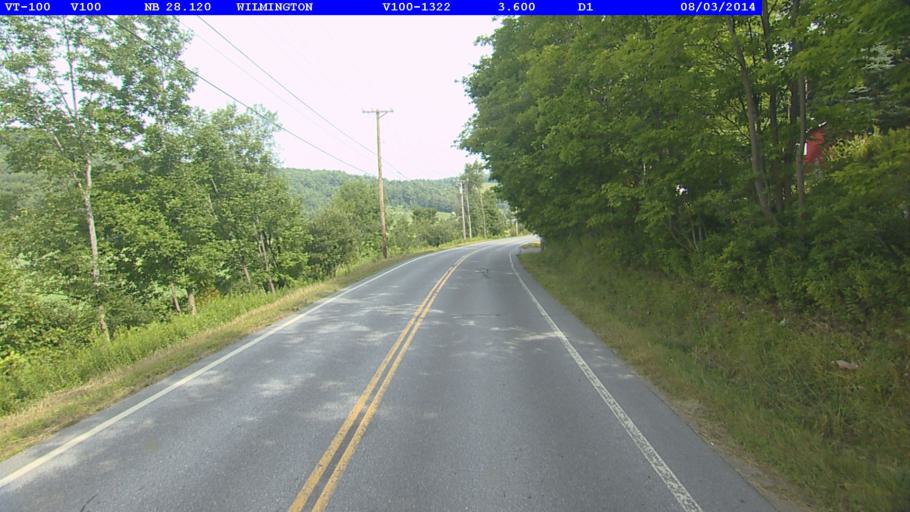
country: US
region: Vermont
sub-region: Windham County
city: Dover
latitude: 42.8813
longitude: -72.8646
